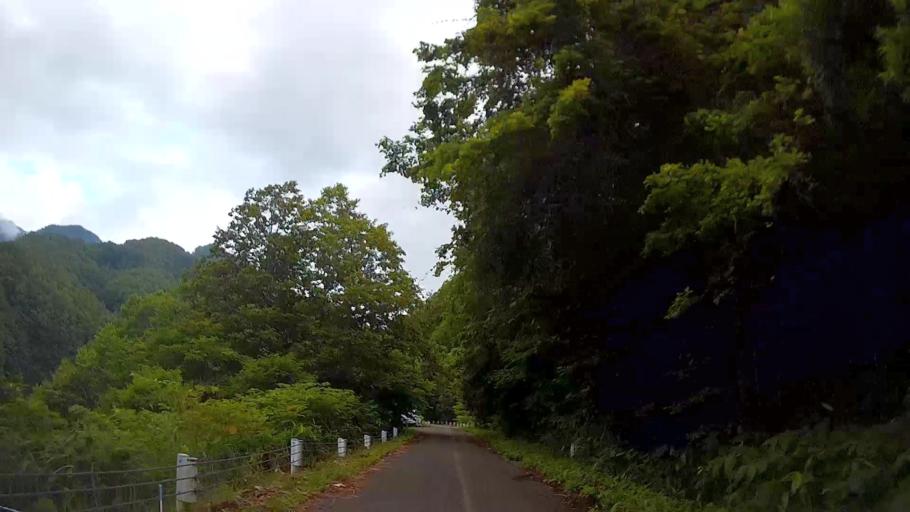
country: JP
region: Hokkaido
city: Nanae
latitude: 42.0621
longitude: 140.5010
